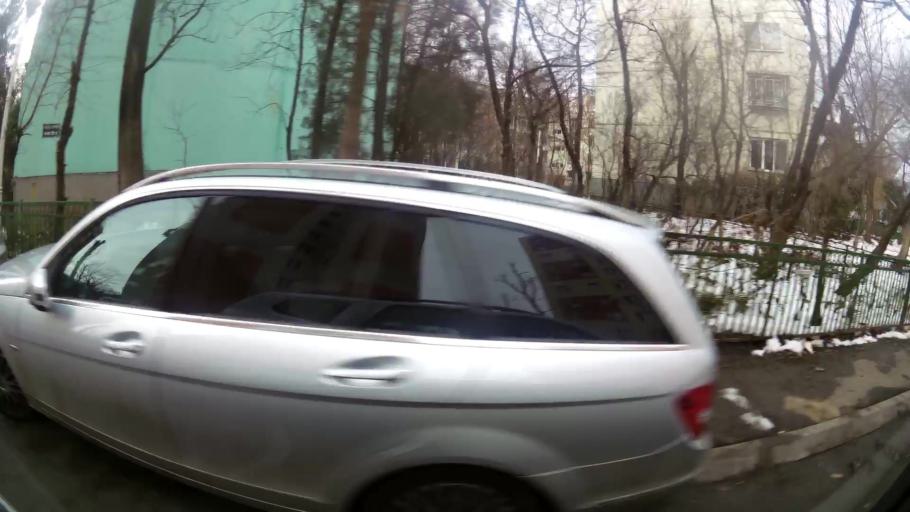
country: RO
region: Bucuresti
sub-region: Municipiul Bucuresti
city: Bucuresti
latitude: 44.4021
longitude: 26.0526
